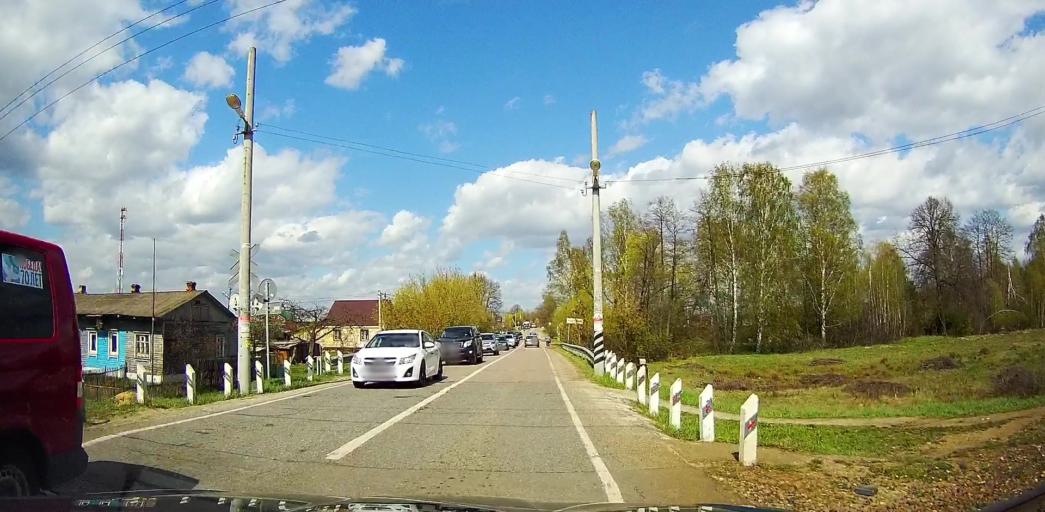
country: RU
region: Moskovskaya
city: Davydovo
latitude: 55.5731
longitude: 38.8192
